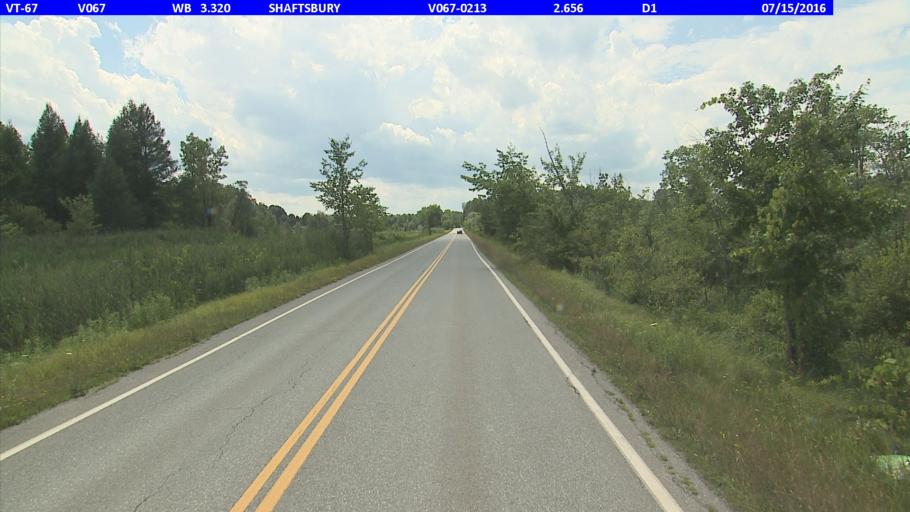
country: US
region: Vermont
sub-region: Bennington County
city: North Bennington
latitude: 42.9417
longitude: -73.2254
